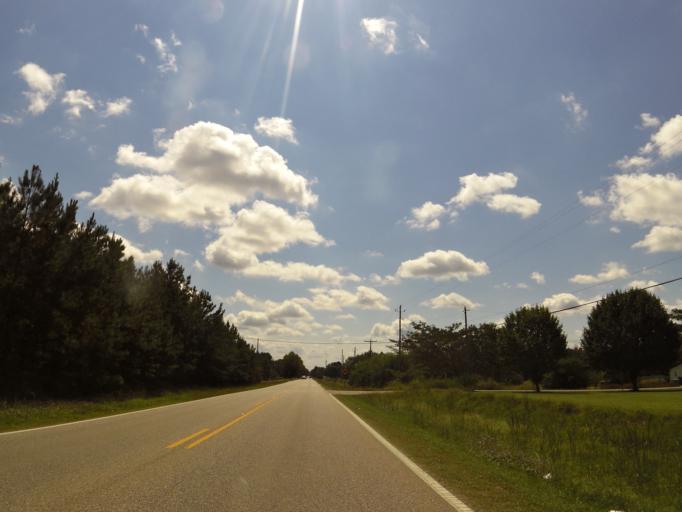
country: US
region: Alabama
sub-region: Dallas County
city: Selma
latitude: 32.4284
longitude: -87.0833
